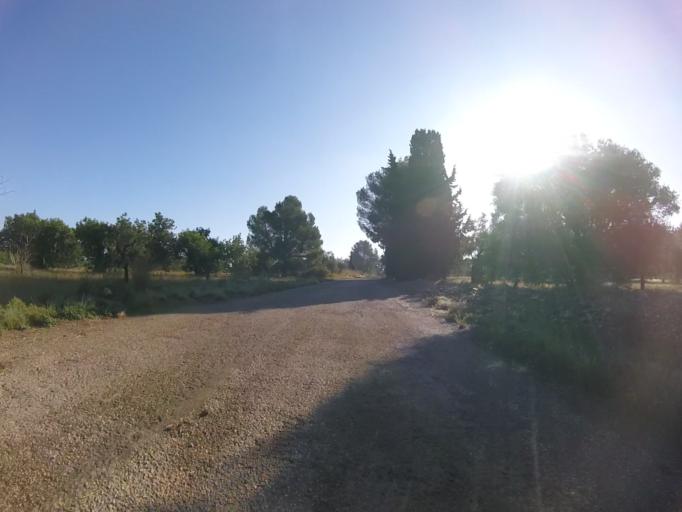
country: ES
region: Valencia
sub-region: Provincia de Castello
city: Peniscola
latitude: 40.3912
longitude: 0.3675
